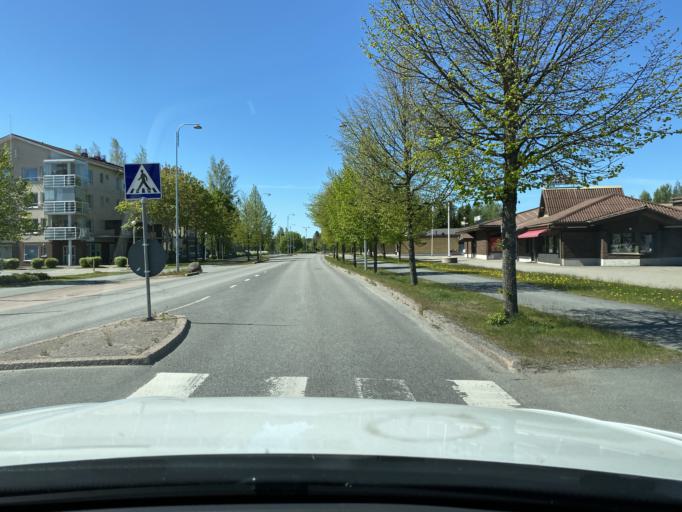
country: FI
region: Satakunta
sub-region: Rauma
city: Eura
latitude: 61.1301
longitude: 22.1386
